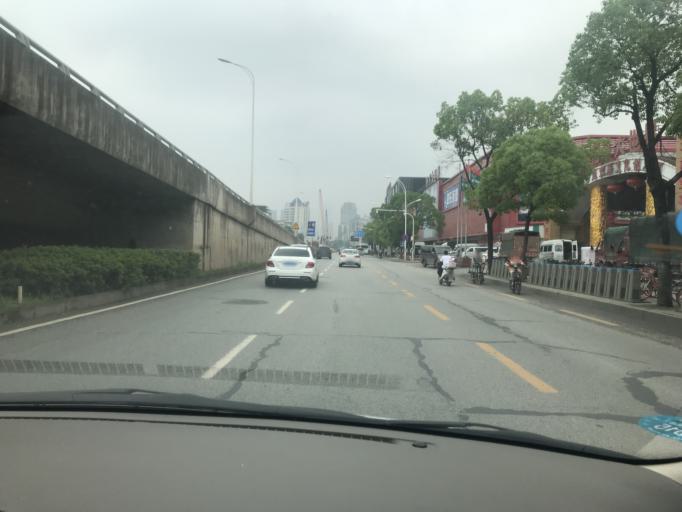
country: CN
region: Hubei
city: Heping
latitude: 30.6133
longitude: 114.3503
